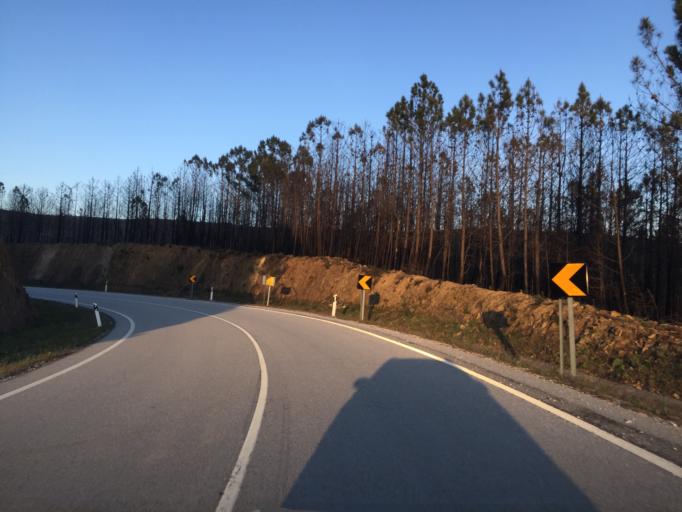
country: PT
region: Coimbra
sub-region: Pampilhosa da Serra
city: Pampilhosa da Serra
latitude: 40.0986
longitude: -7.9965
